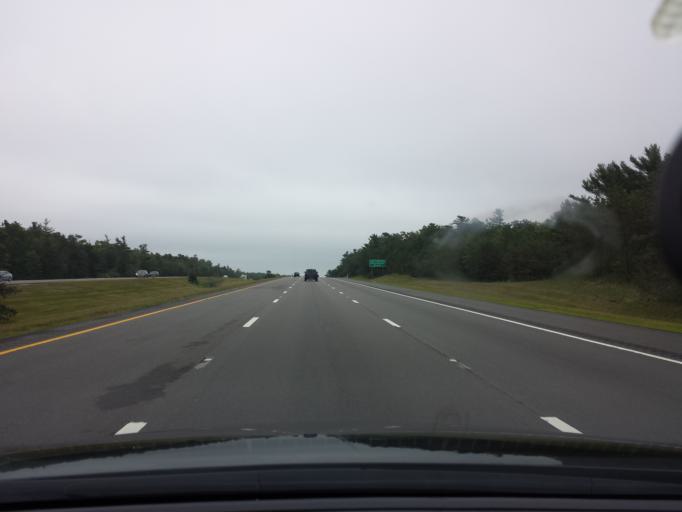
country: US
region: Massachusetts
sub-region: Plymouth County
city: Onset
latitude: 41.7693
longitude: -70.6470
